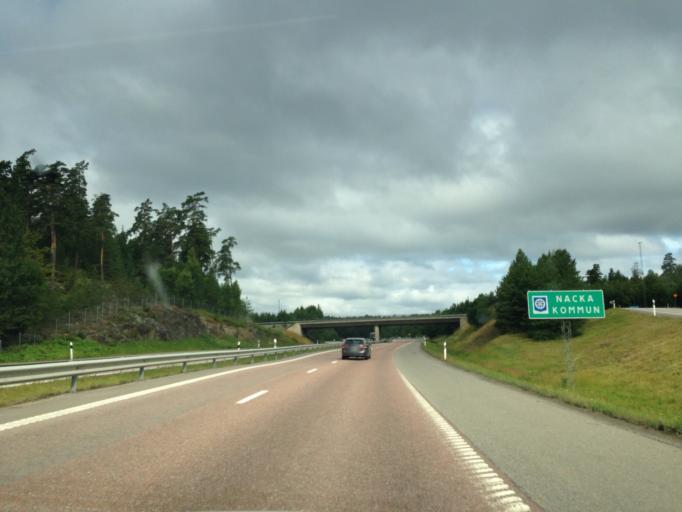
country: SE
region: Stockholm
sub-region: Nacka Kommun
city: Boo
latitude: 59.3252
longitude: 18.3339
